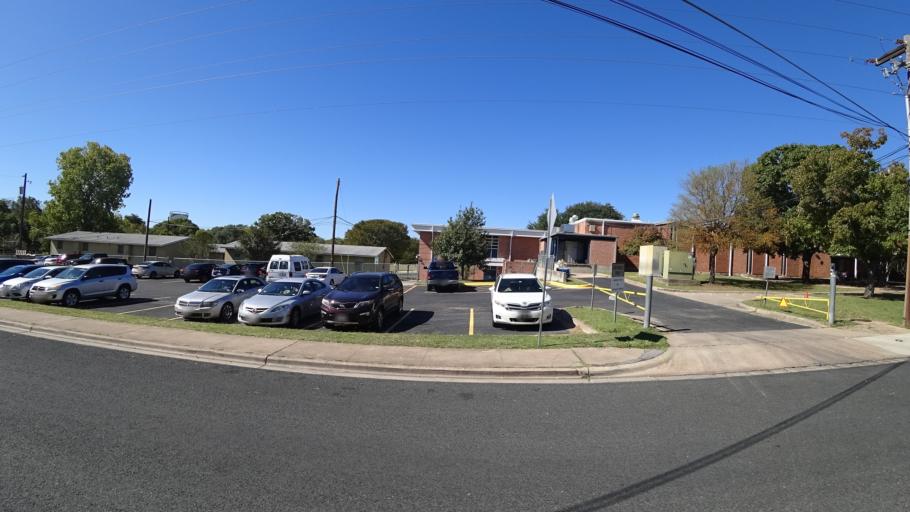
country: US
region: Texas
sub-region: Travis County
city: Austin
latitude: 30.3069
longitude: -97.6897
